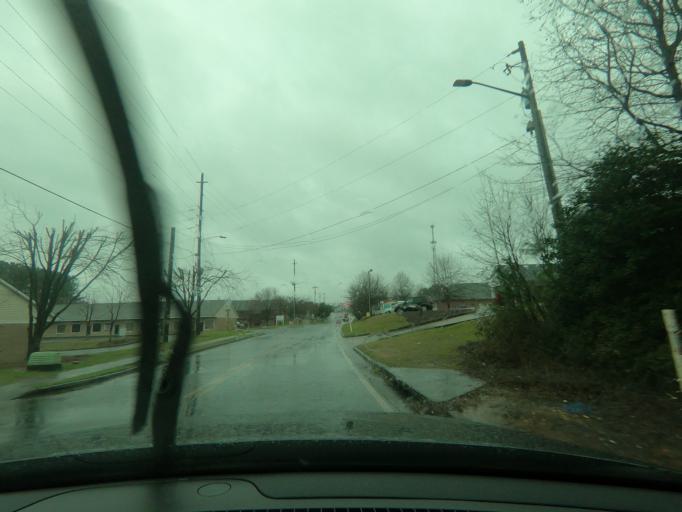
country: US
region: Georgia
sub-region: Cobb County
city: Acworth
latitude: 34.0736
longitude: -84.6496
